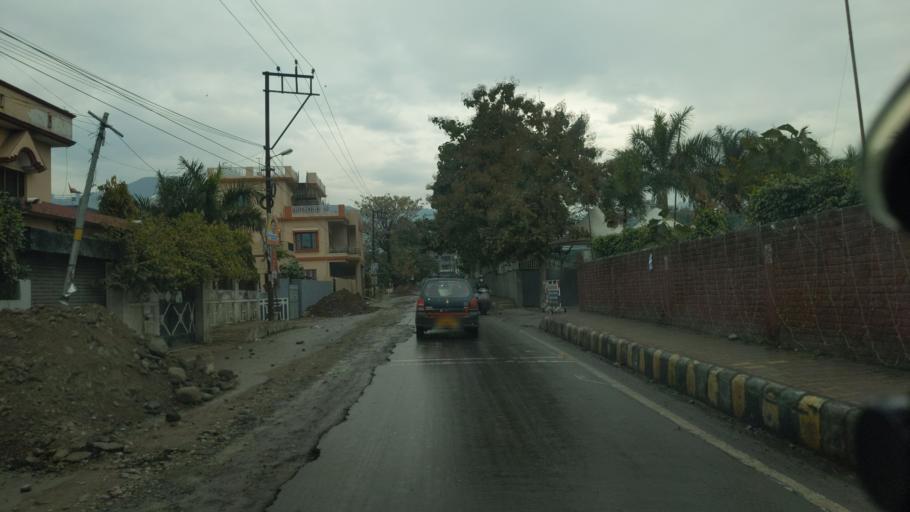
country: IN
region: Uttarakhand
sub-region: Naini Tal
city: Haldwani
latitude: 29.2449
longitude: 79.5331
